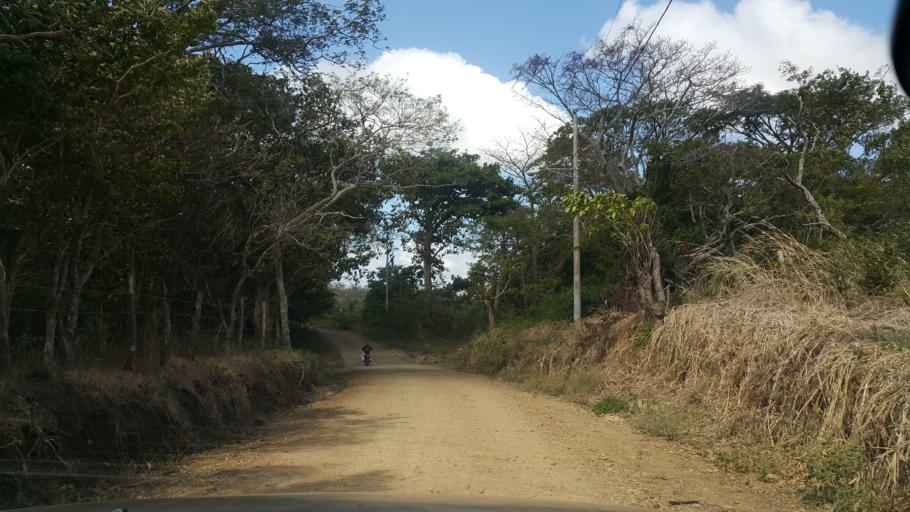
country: NI
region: Rivas
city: San Juan del Sur
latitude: 11.3077
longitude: -85.8355
